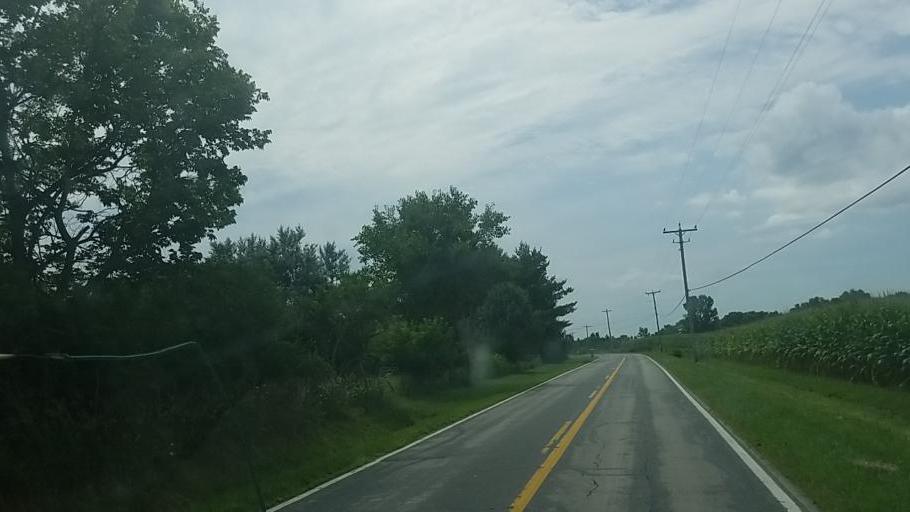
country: US
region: Ohio
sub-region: Delaware County
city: Sunbury
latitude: 40.1773
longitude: -82.8271
